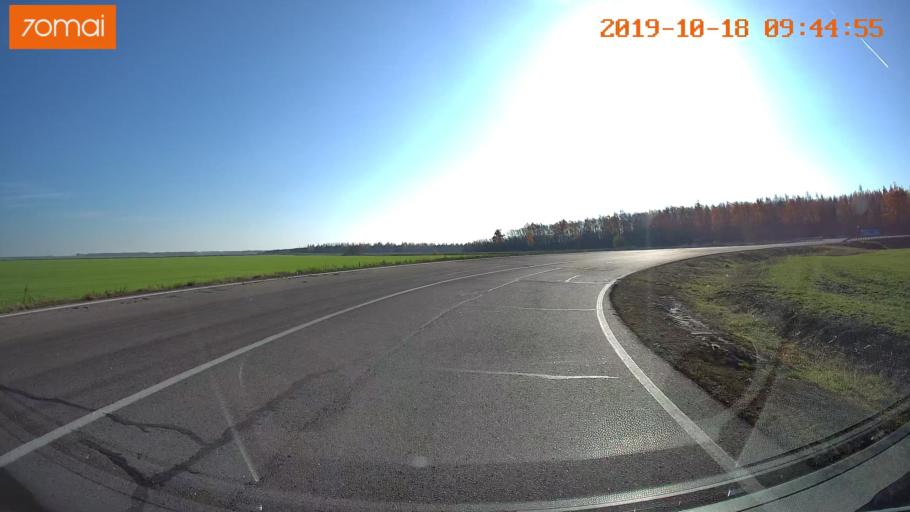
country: RU
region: Tula
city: Kazachka
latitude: 53.3138
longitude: 38.1825
